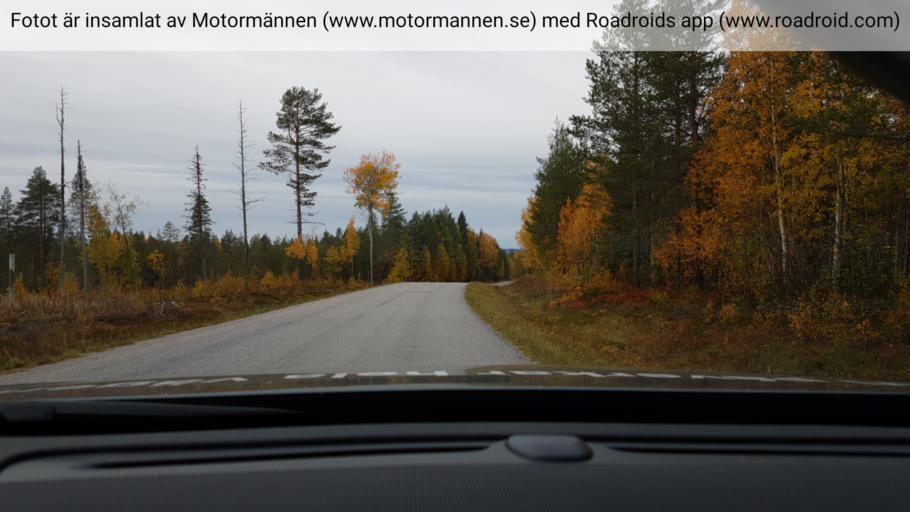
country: SE
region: Norrbotten
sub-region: Overkalix Kommun
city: OEverkalix
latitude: 66.2590
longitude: 23.0436
